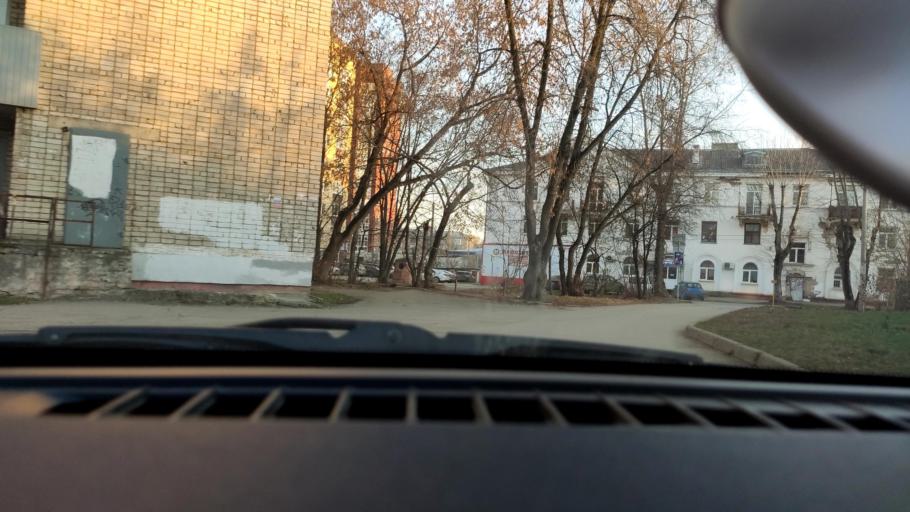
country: RU
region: Perm
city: Perm
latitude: 57.9870
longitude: 56.2050
